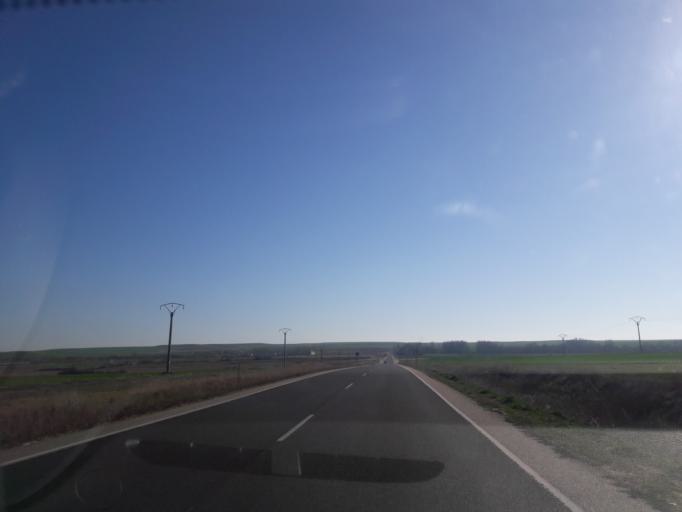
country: ES
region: Castille and Leon
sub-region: Provincia de Salamanca
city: Penarandilla
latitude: 40.8704
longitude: -5.3831
